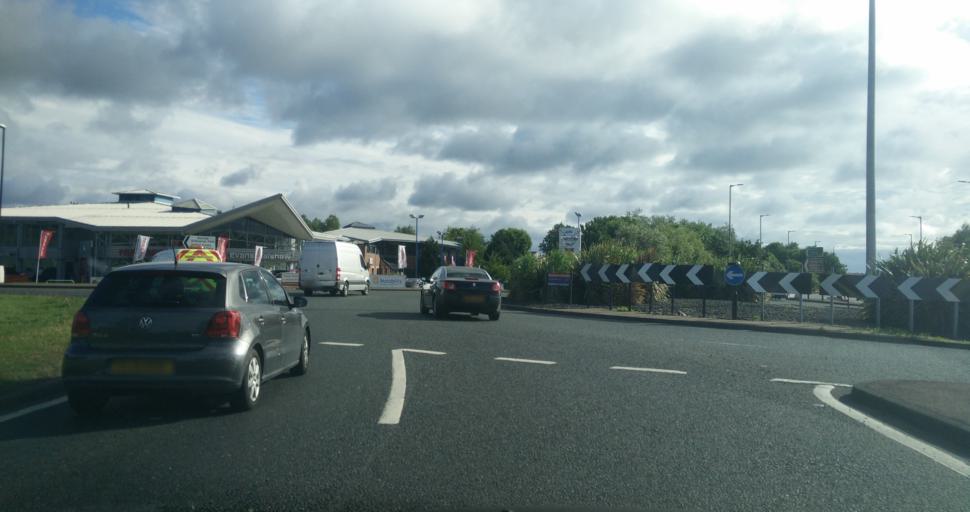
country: GB
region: England
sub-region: South Tyneside
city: The Boldons
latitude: 54.9110
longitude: -1.4551
